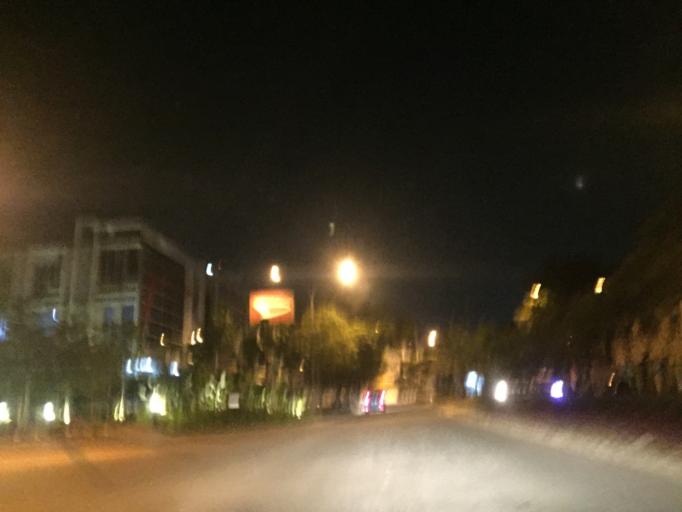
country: ID
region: Banten
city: Curug
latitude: -6.2447
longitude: 106.6130
